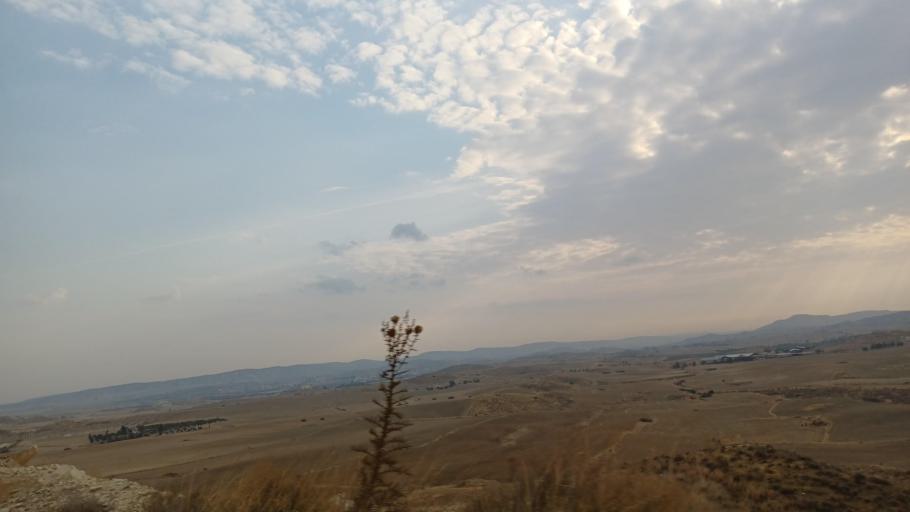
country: CY
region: Larnaka
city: Troulloi
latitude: 35.0228
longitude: 33.5747
